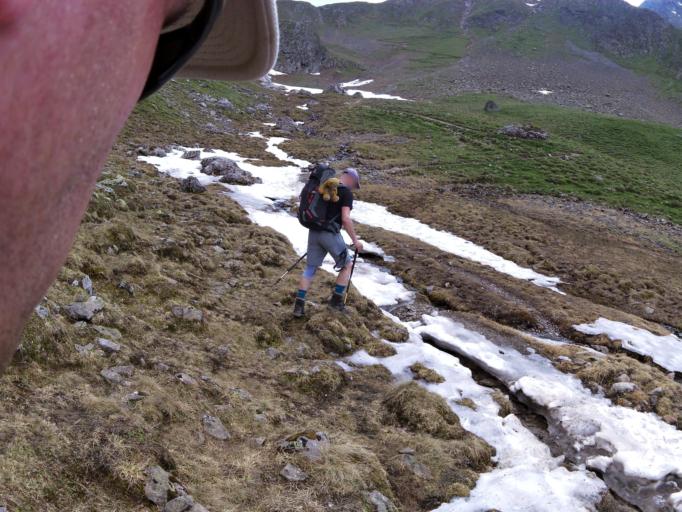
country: AT
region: Tyrol
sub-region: Politischer Bezirk Innsbruck Land
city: Gschnitz
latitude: 47.0482
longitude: 11.3126
